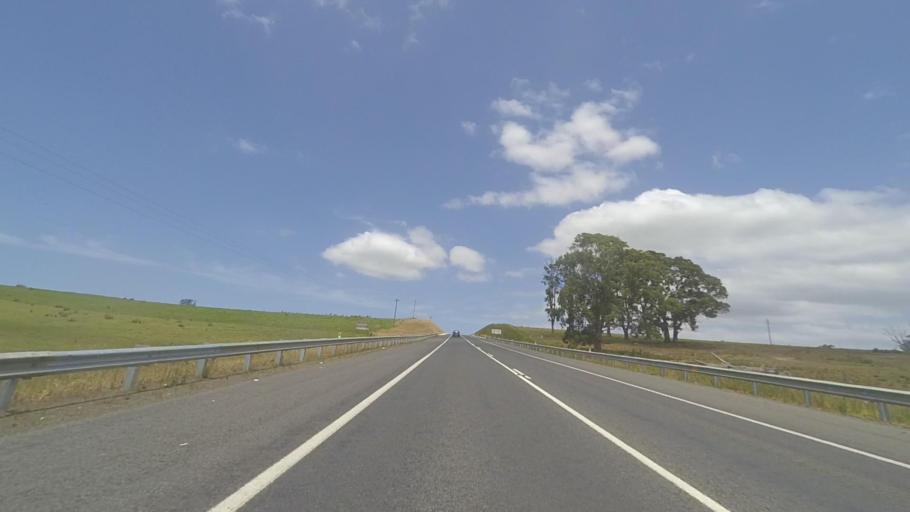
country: AU
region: New South Wales
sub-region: Shoalhaven Shire
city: Milton
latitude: -35.2840
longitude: 150.4219
